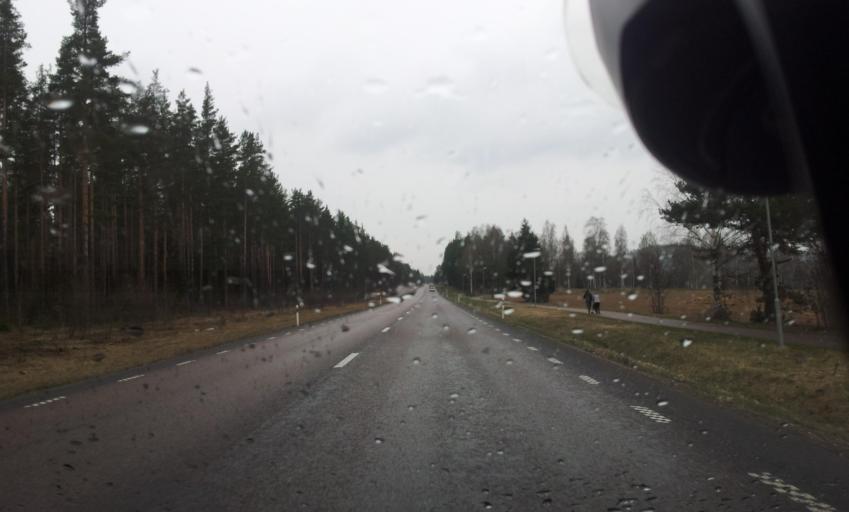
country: SE
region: Dalarna
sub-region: Borlange Kommun
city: Borlaenge
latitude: 60.5196
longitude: 15.3655
